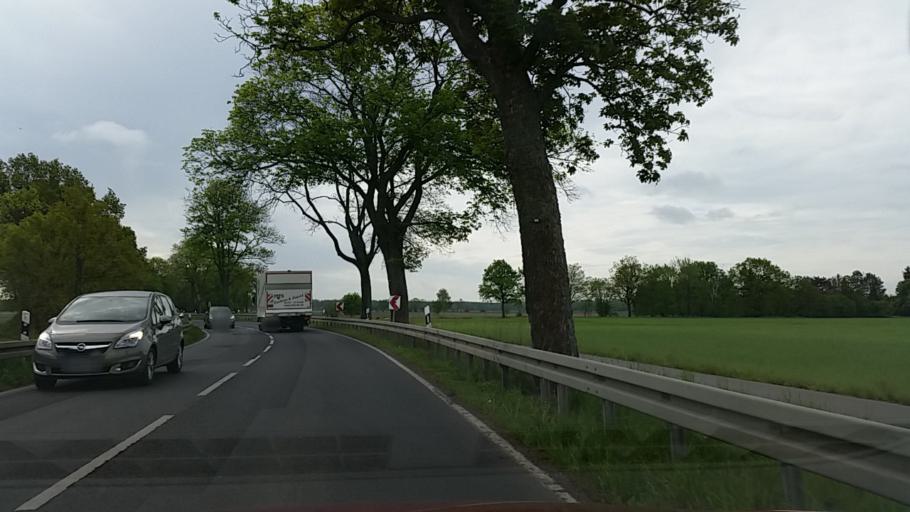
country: DE
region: Brandenburg
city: Velten
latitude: 52.6670
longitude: 13.1609
